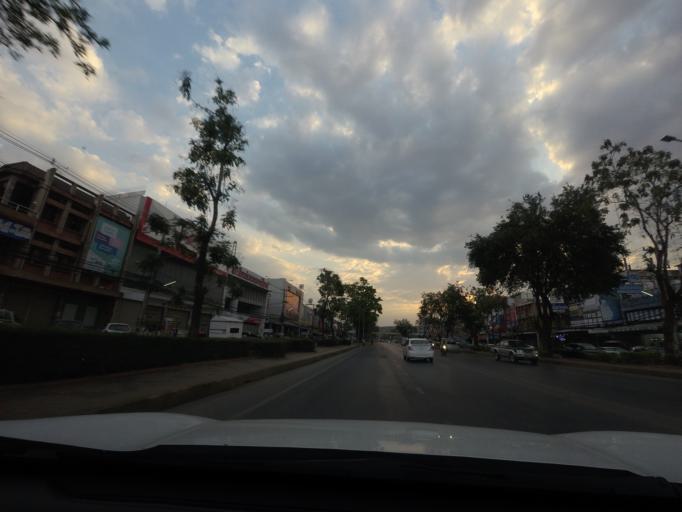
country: TH
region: Nakhon Ratchasima
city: Pak Chong
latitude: 14.7071
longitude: 101.4172
